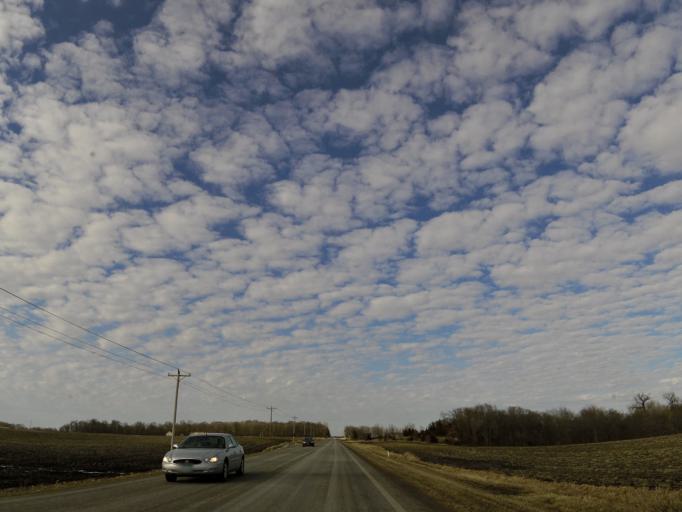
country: US
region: Minnesota
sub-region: Le Sueur County
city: New Prague
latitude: 44.5904
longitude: -93.5576
